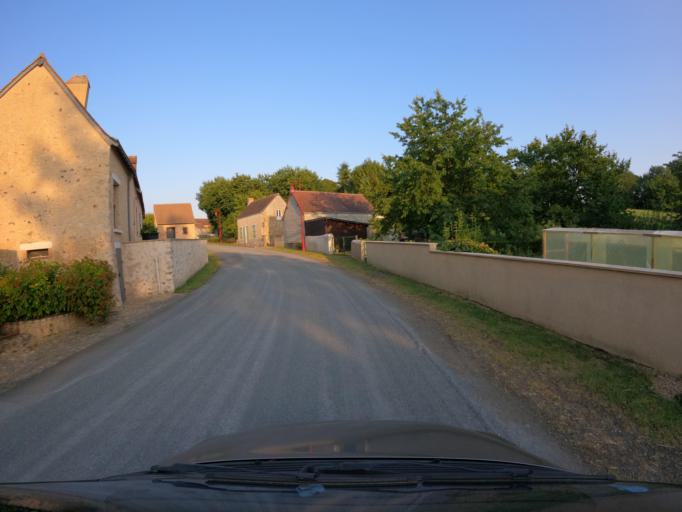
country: FR
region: Pays de la Loire
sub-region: Departement de la Sarthe
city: Parce-sur-Sarthe
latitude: 47.9023
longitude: -0.2220
